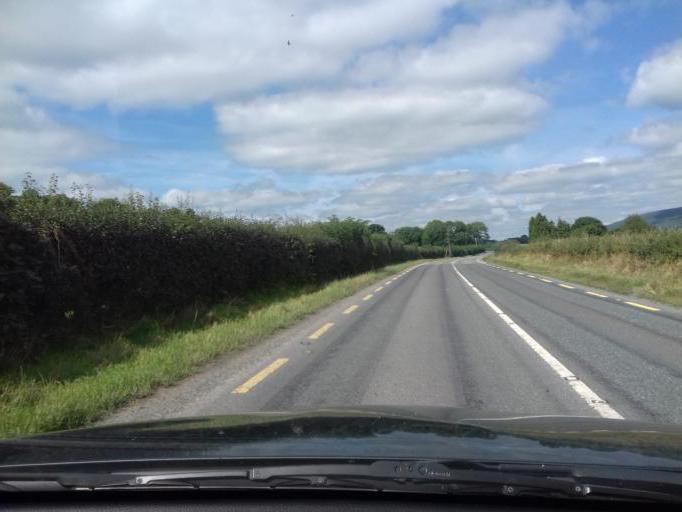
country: IE
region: Leinster
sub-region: Wicklow
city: Baltinglass
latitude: 53.0041
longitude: -6.6441
